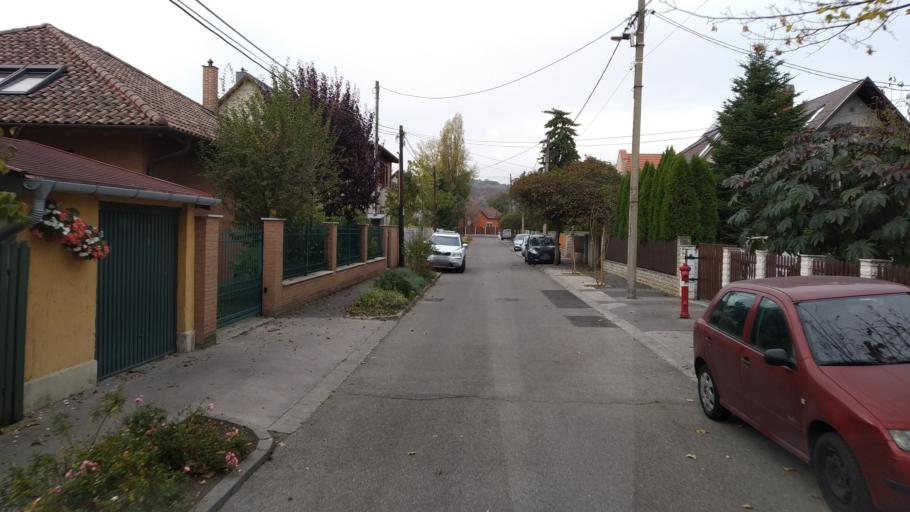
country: HU
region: Pest
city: Budakalasz
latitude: 47.5859
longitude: 19.0531
